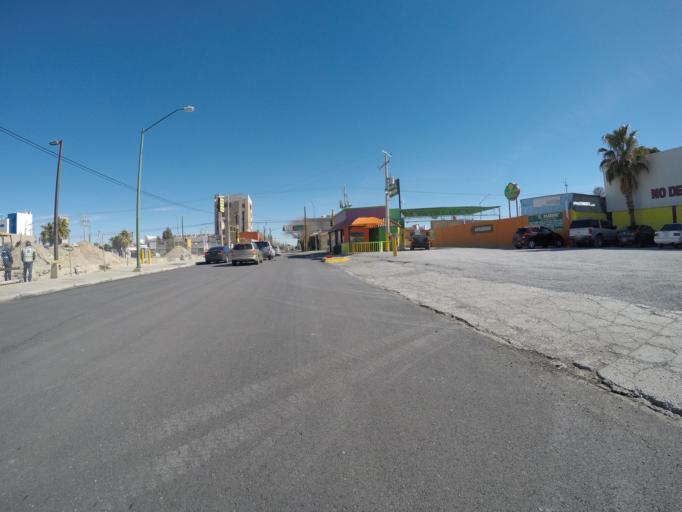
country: MX
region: Chihuahua
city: Ciudad Juarez
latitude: 31.7401
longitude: -106.4588
